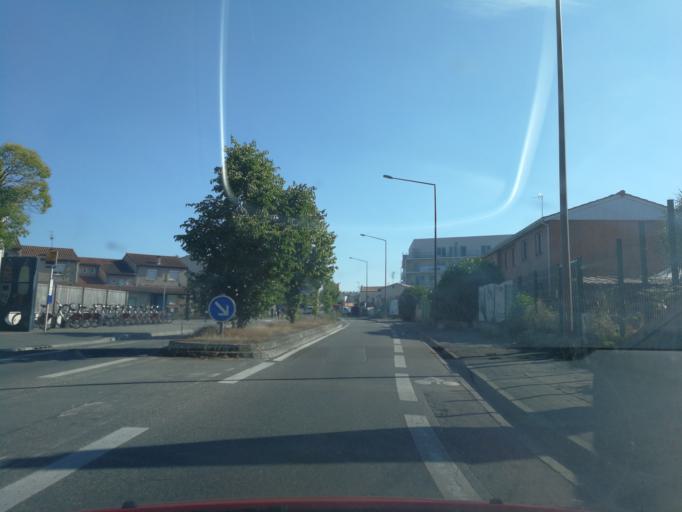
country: FR
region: Midi-Pyrenees
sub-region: Departement de la Haute-Garonne
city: Toulouse
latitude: 43.6245
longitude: 1.4546
